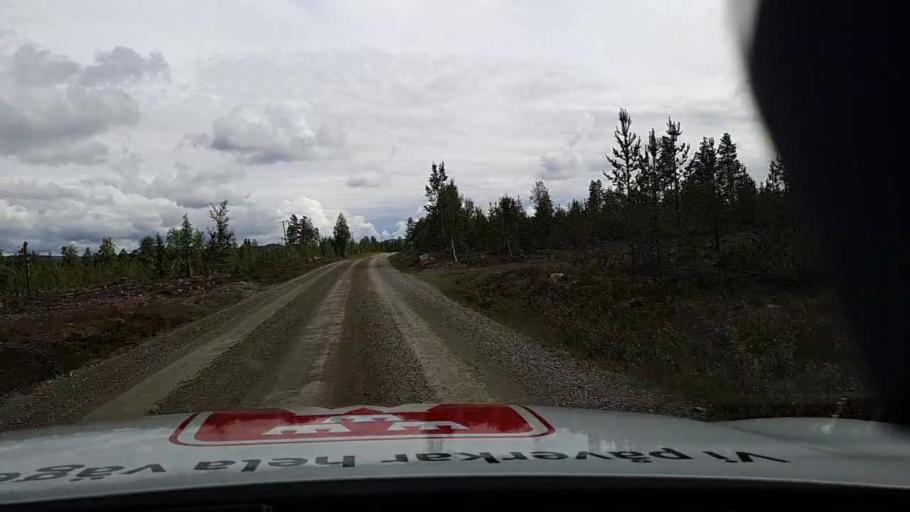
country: SE
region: Jaemtland
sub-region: Are Kommun
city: Jarpen
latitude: 62.5077
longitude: 13.4958
